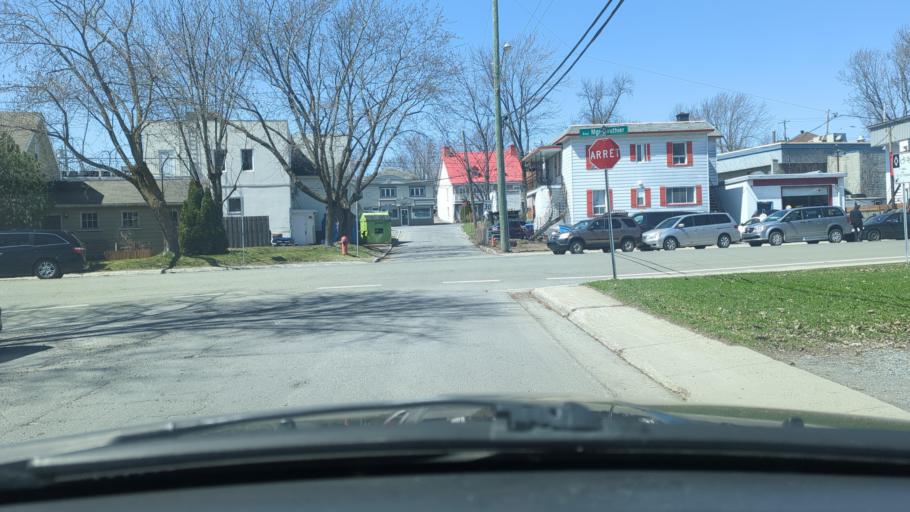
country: CA
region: Quebec
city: Quebec
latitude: 46.8496
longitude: -71.2101
